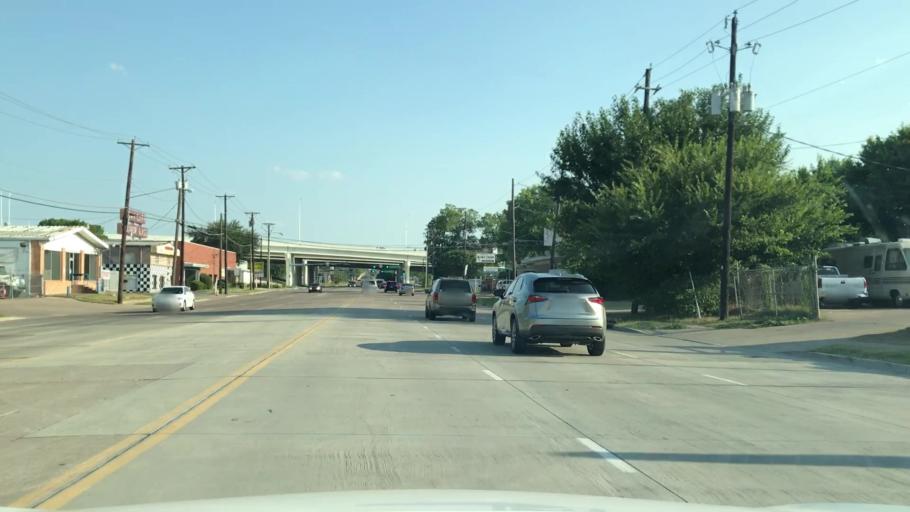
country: US
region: Texas
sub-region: Dallas County
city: Dallas
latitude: 32.7717
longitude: -96.8229
